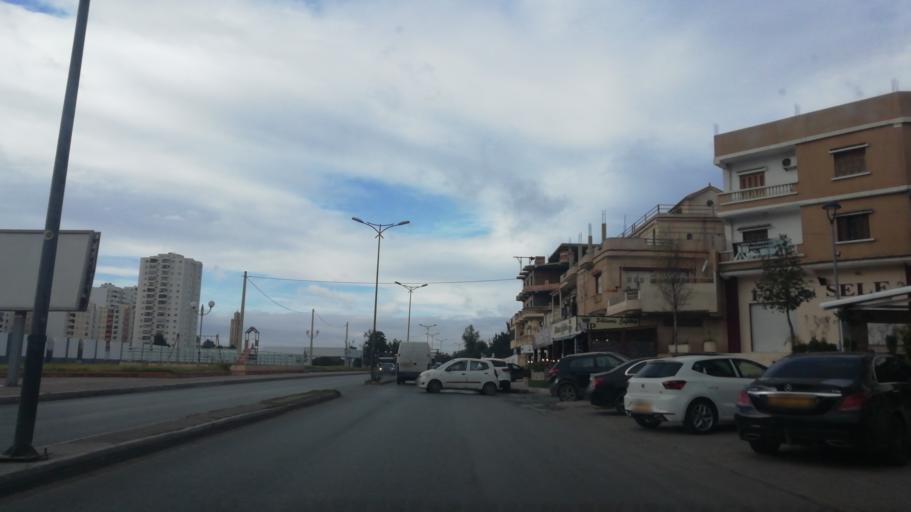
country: DZ
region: Oran
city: Bir el Djir
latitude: 35.7143
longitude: -0.5809
